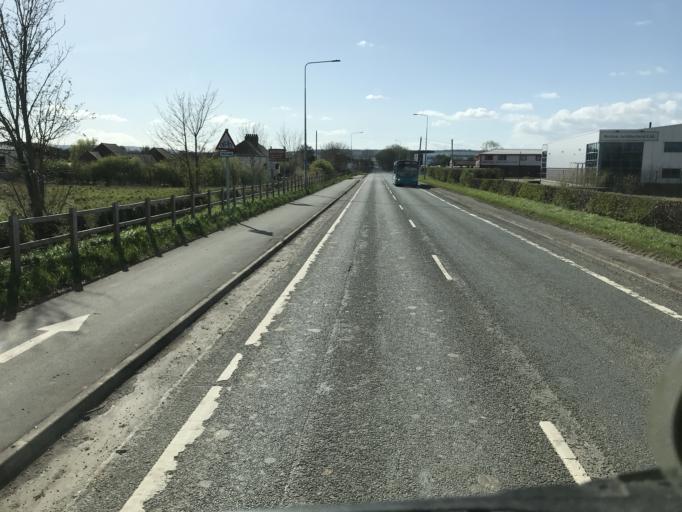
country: GB
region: England
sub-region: Cheshire West and Chester
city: Blacon
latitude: 53.1734
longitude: -2.9591
